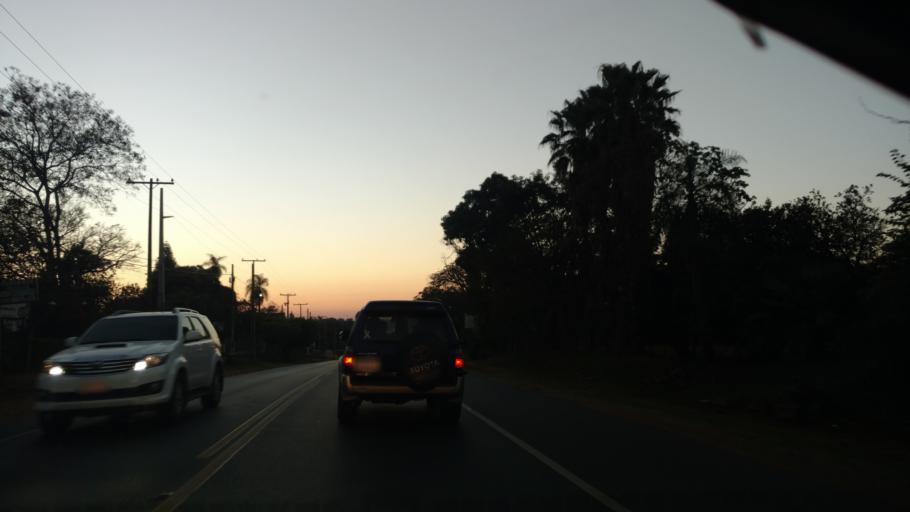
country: PY
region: Central
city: Guarambare
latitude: -25.4791
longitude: -57.4107
